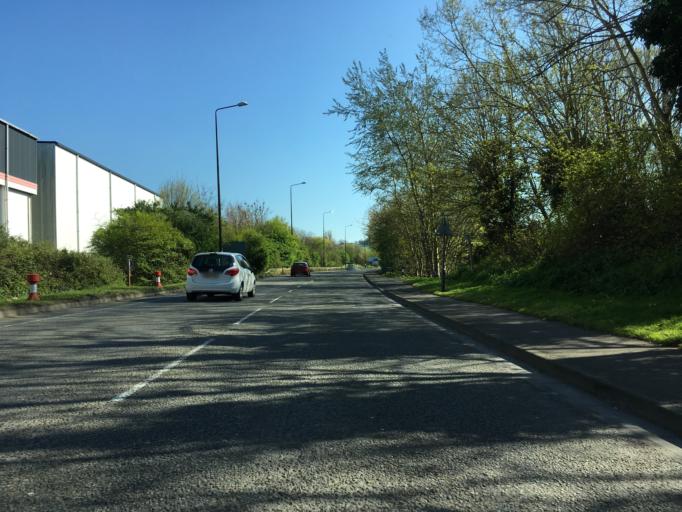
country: GB
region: England
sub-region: North Somerset
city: Easton-in-Gordano
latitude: 51.4819
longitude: -2.7125
